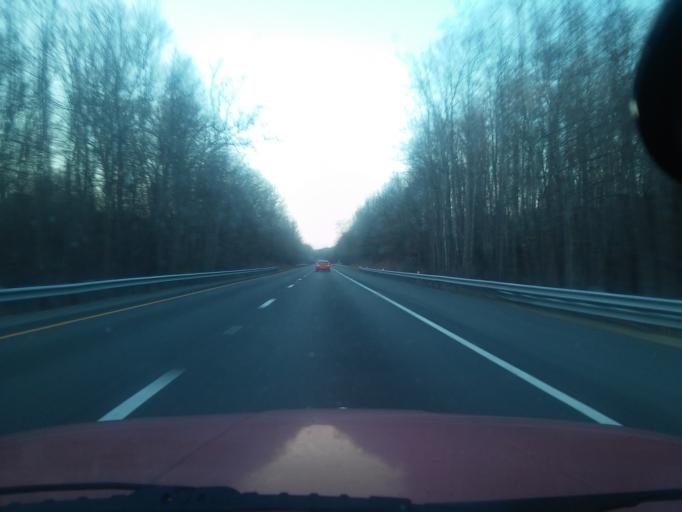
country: US
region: Virginia
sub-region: Goochland County
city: Goochland
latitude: 37.7328
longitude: -77.8265
